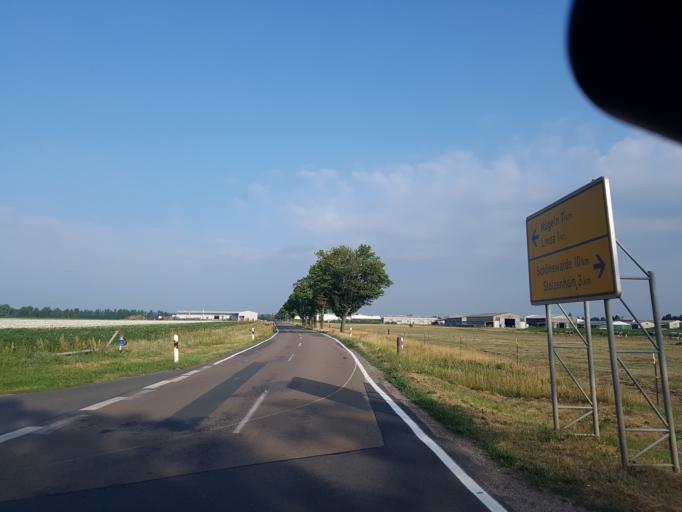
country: DE
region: Saxony-Anhalt
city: Holzdorf
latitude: 51.8520
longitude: 13.1177
